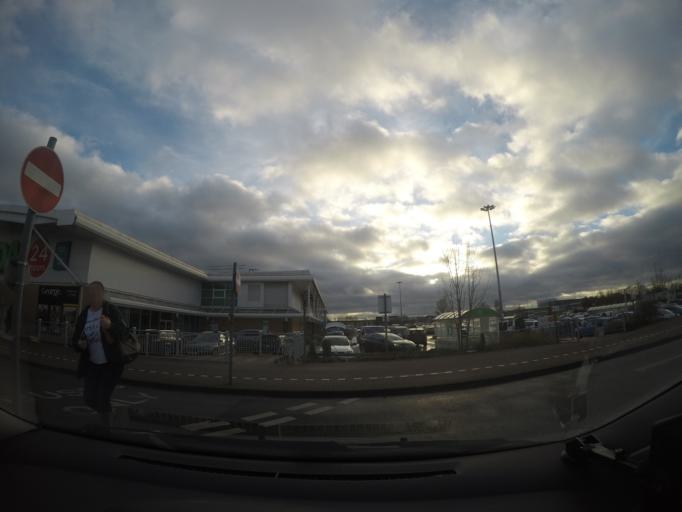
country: GB
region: England
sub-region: City of York
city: Huntington
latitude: 53.9872
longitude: -1.0440
